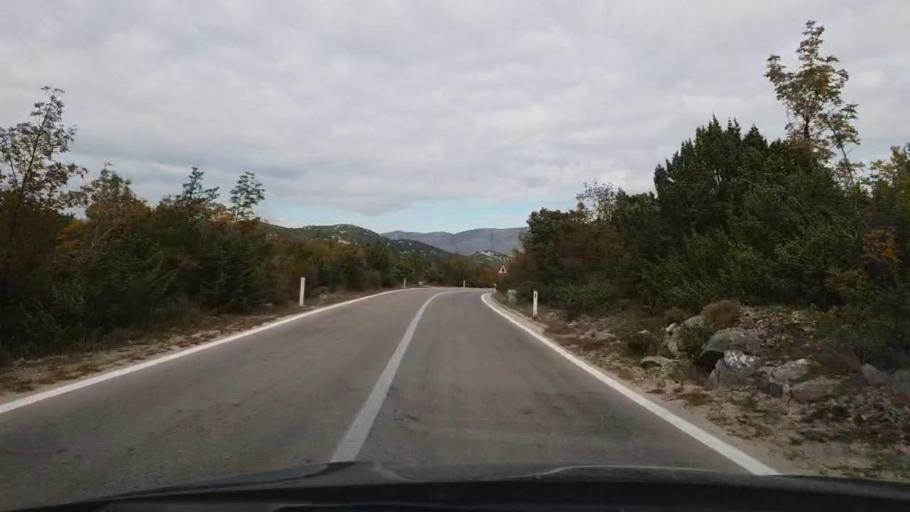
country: HR
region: Dubrovacko-Neretvanska
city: Cibaca
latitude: 42.6762
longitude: 18.2355
